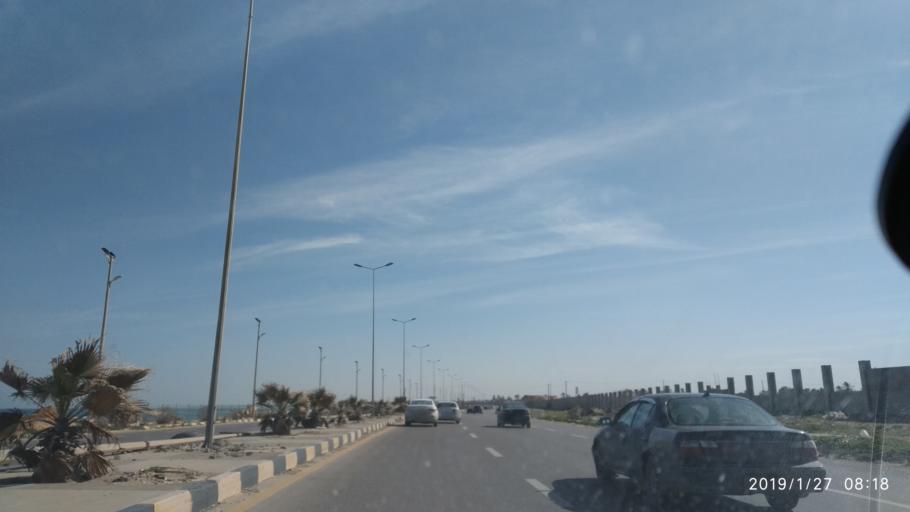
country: LY
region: Tripoli
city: Tagiura
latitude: 32.9062
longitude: 13.2957
